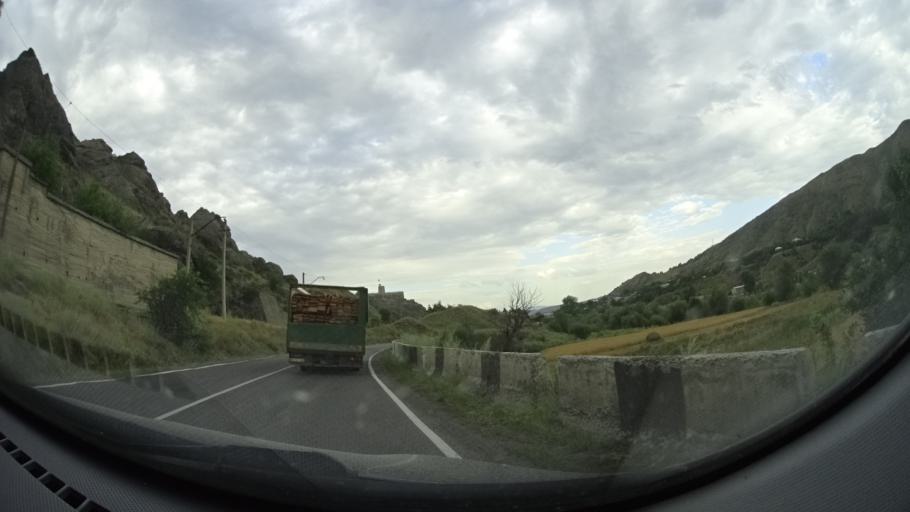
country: GE
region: Samtskhe-Javakheti
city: Akhaltsikhe
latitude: 41.6408
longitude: 42.9674
